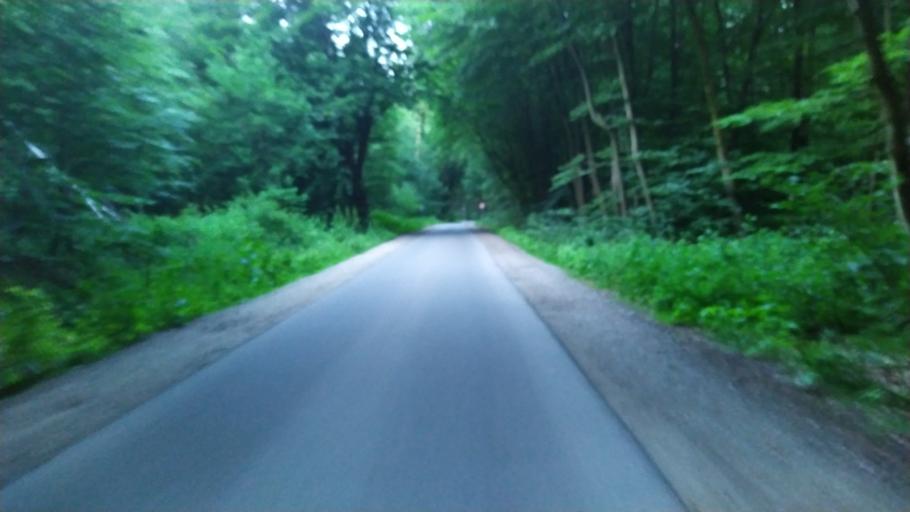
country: DE
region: Lower Saxony
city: Deinstedt
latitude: 53.4946
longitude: 9.2447
